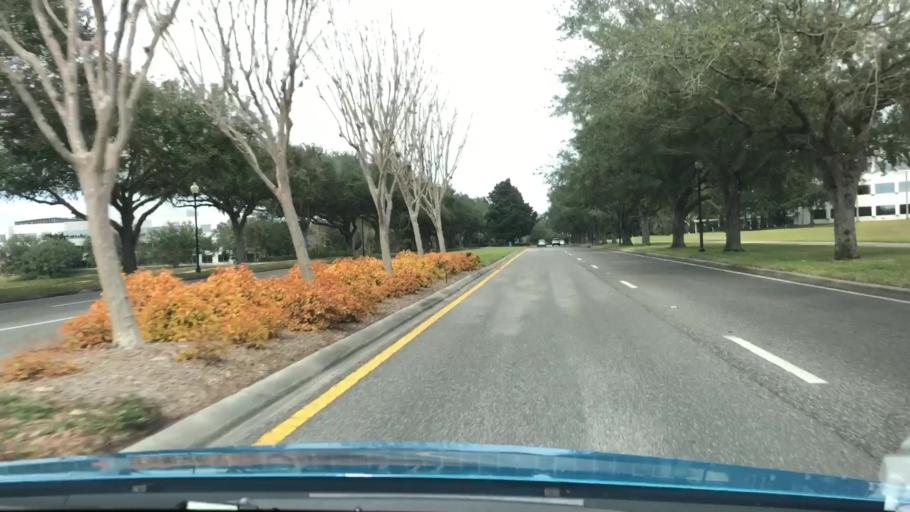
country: US
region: Florida
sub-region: Seminole County
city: Heathrow
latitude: 28.7731
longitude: -81.3588
